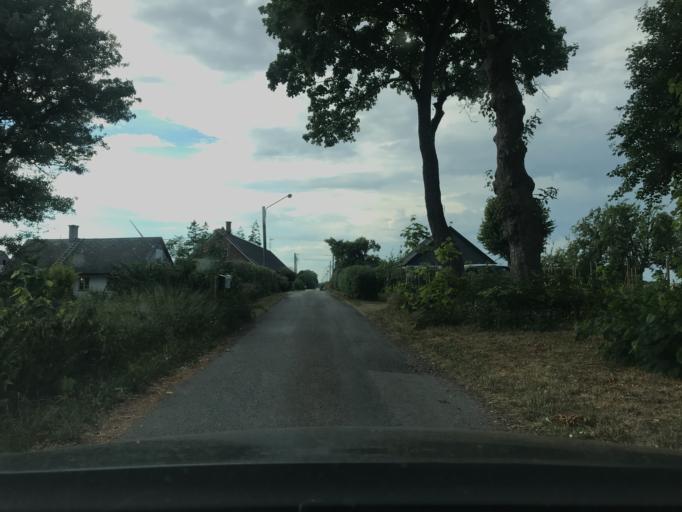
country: SE
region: Skane
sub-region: Simrishamns Kommun
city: Kivik
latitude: 55.5265
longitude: 14.1654
